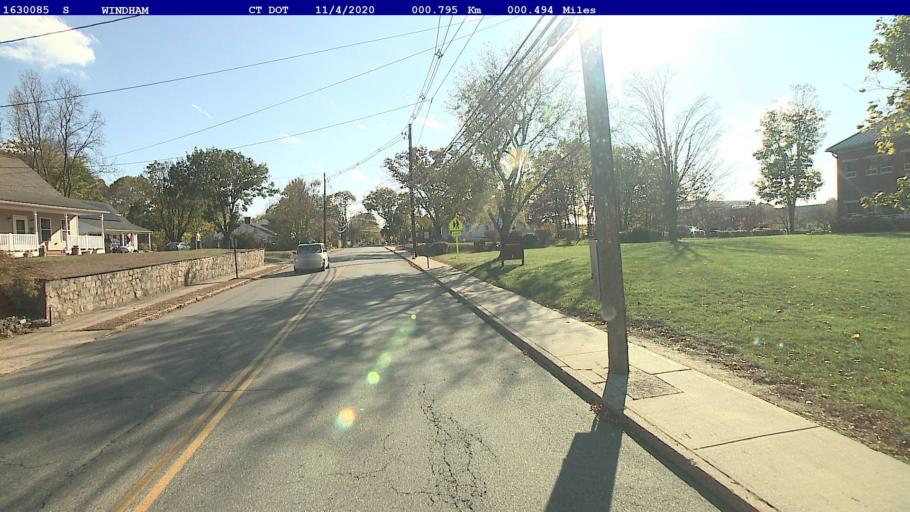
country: US
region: Connecticut
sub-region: Windham County
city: Willimantic
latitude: 41.7212
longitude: -72.2158
